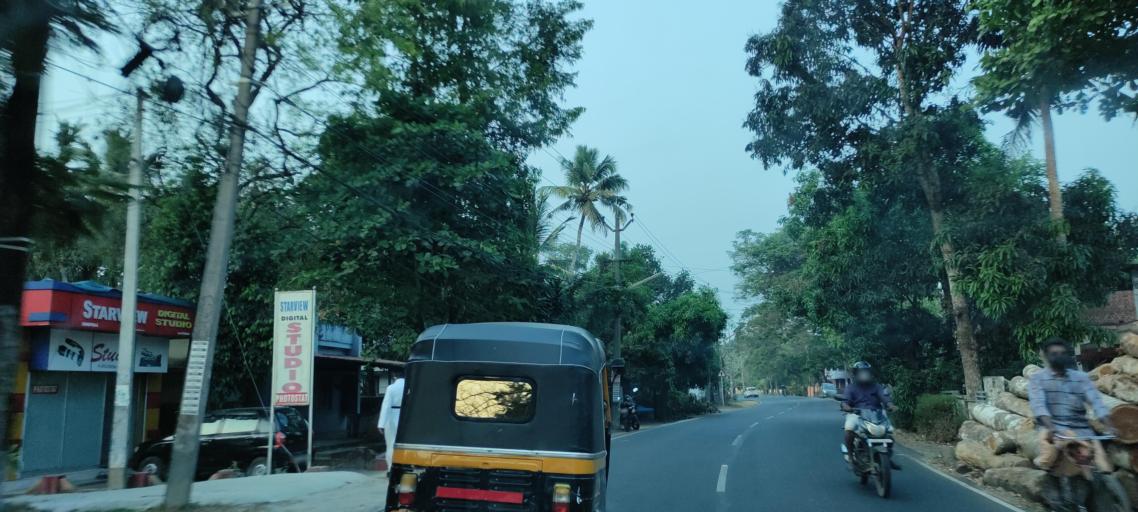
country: IN
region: Kerala
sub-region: Alappuzha
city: Mavelikara
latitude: 9.2921
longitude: 76.5326
